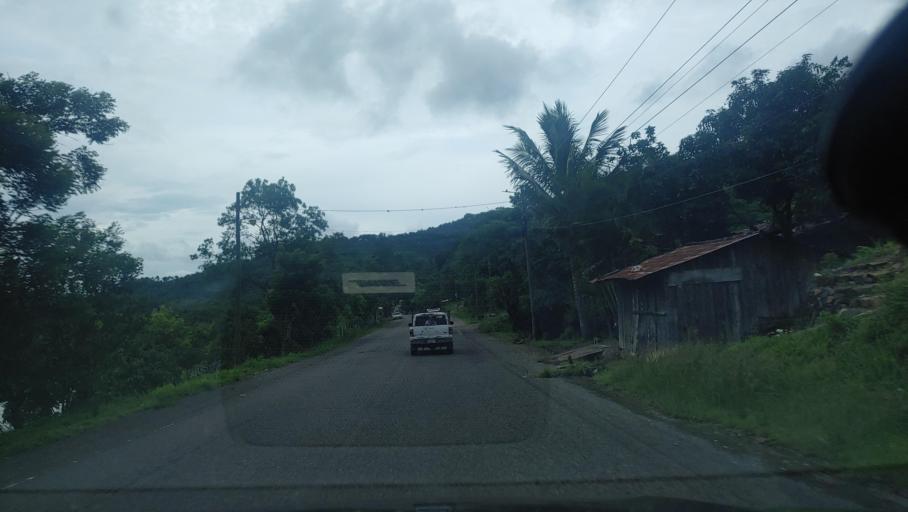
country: HN
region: Choluteca
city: San Marcos de Colon
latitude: 13.3784
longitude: -86.8762
